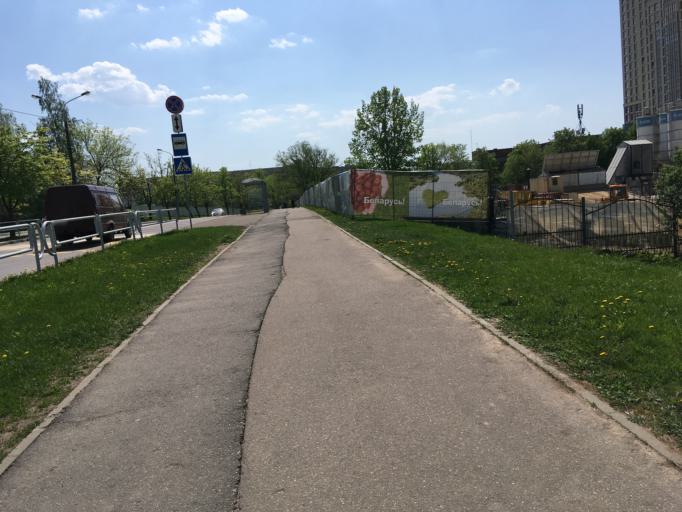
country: BY
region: Minsk
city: Minsk
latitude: 53.9234
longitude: 27.6278
